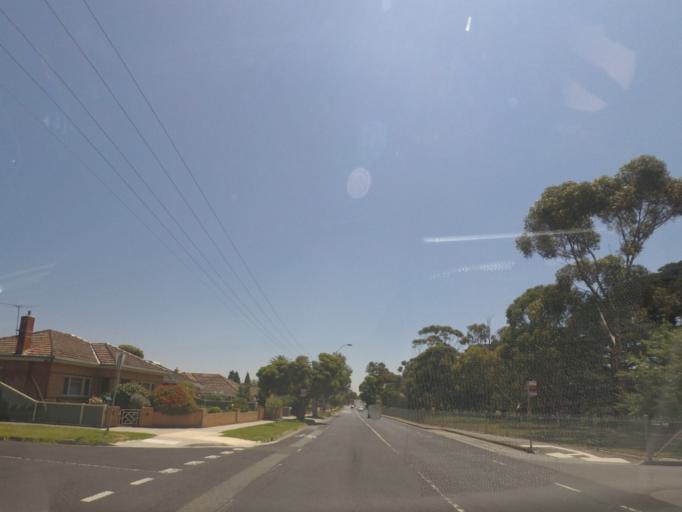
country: AU
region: Victoria
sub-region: Moreland
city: Fawkner
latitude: -37.7184
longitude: 144.9547
